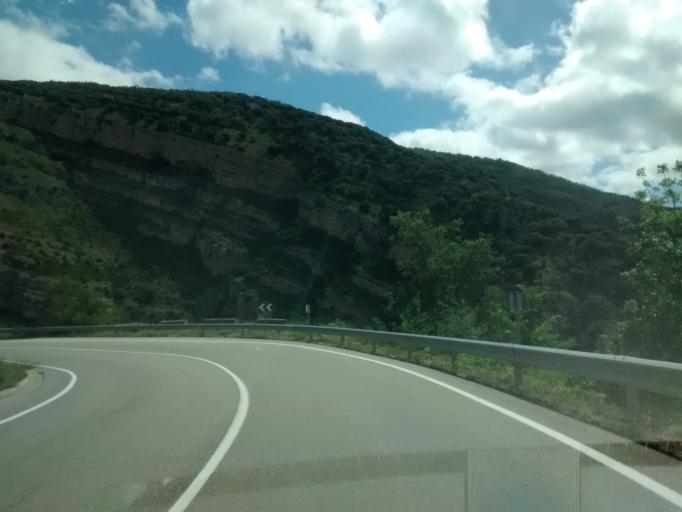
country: ES
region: La Rioja
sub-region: Provincia de La Rioja
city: Leza de Rio Leza
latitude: 42.3084
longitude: -2.4124
